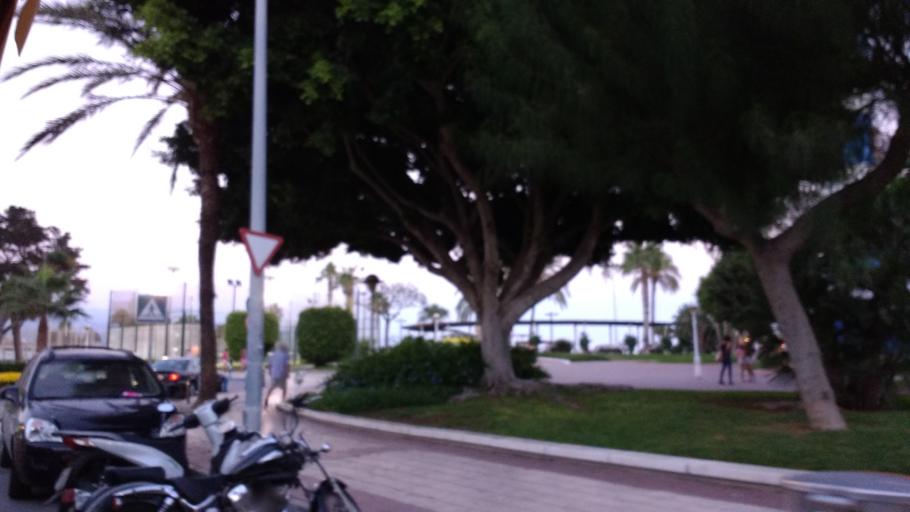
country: ES
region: Andalusia
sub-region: Provincia de Malaga
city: Velez-Malaga
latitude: 36.7352
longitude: -4.0966
